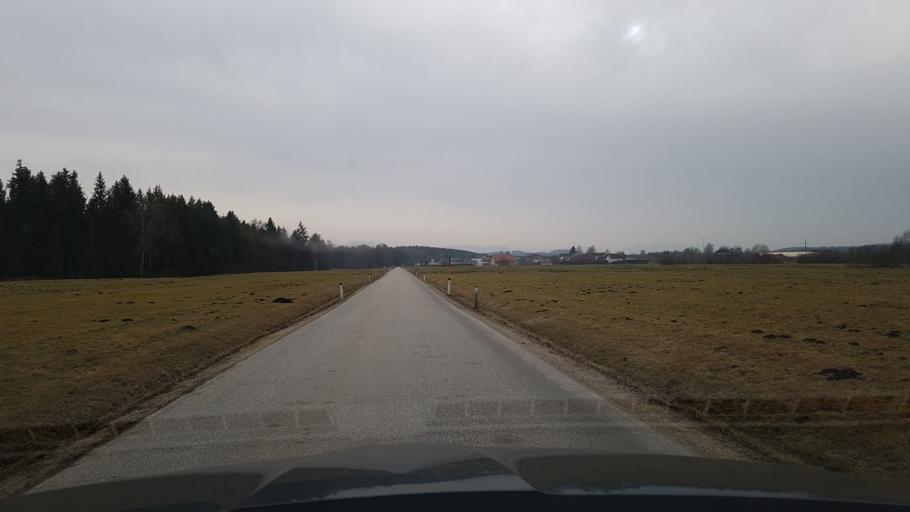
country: AT
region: Salzburg
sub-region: Politischer Bezirk Salzburg-Umgebung
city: Lamprechtshausen
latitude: 48.0516
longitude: 12.9551
